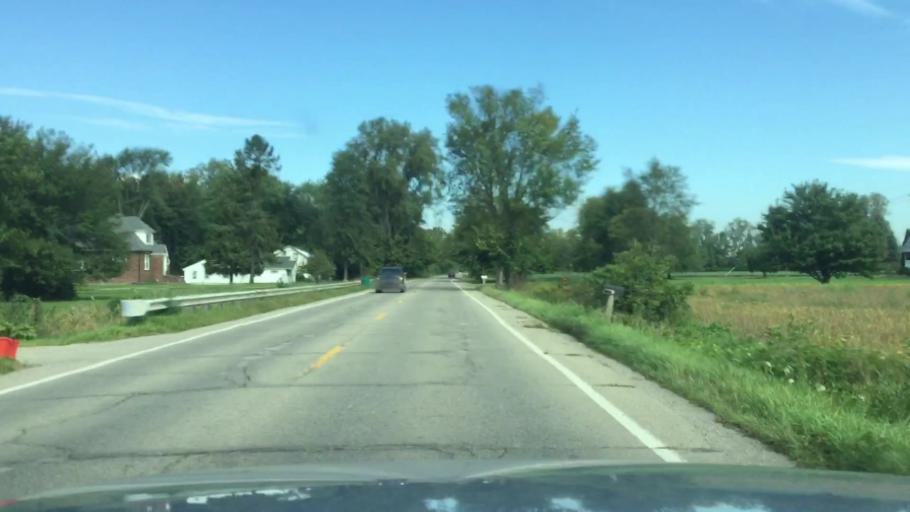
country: US
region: Michigan
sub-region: Wayne County
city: Belleville
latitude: 42.1812
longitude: -83.4831
